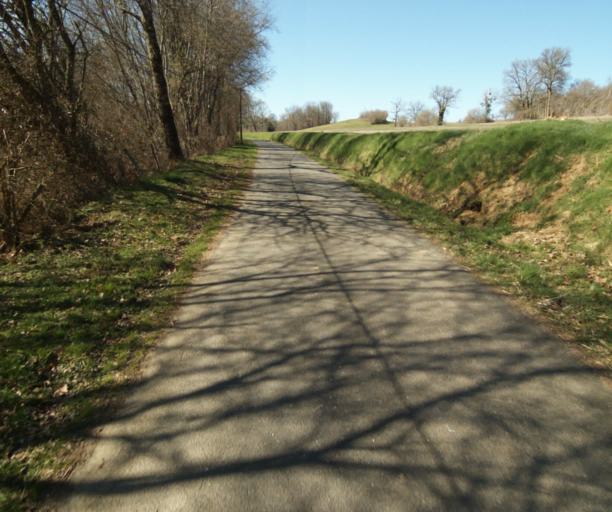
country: FR
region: Limousin
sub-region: Departement de la Correze
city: Chamboulive
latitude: 45.4047
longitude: 1.6400
